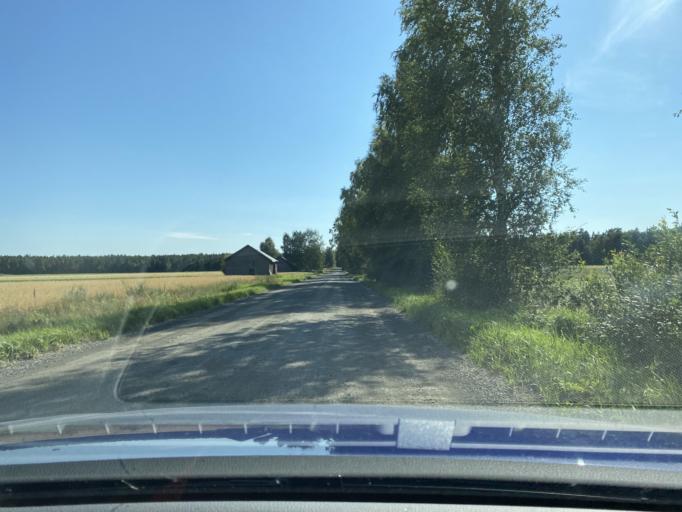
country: FI
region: Satakunta
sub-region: Rauma
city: Kiukainen
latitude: 61.1478
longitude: 22.0005
